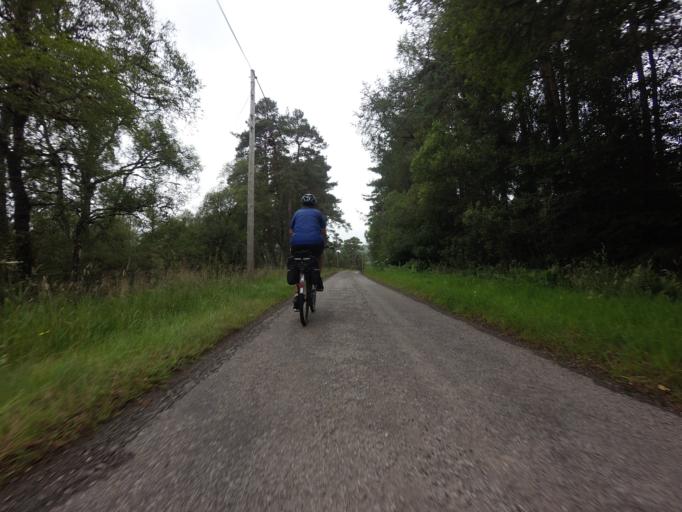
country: GB
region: Scotland
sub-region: Highland
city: Alness
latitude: 57.9872
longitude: -4.4129
